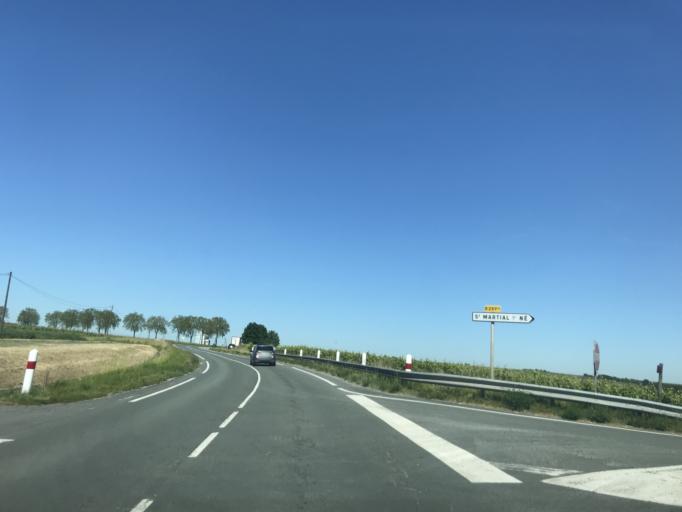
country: FR
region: Poitou-Charentes
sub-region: Departement de la Charente-Maritime
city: Perignac
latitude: 45.5622
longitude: -0.3871
